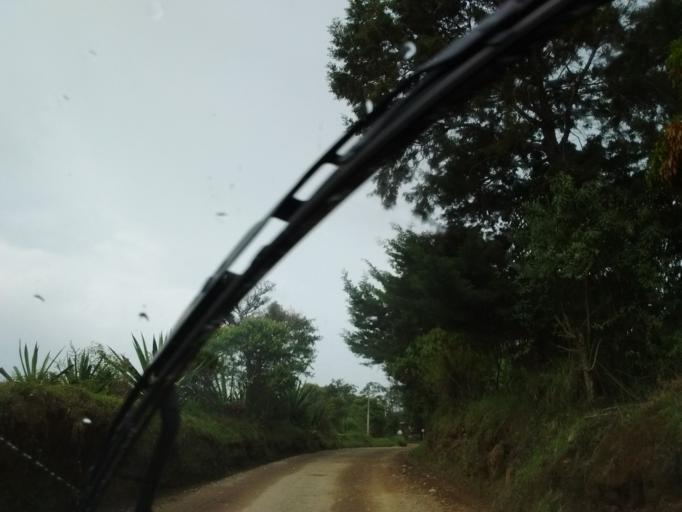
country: CO
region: Cauca
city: Popayan
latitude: 2.5257
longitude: -76.5999
